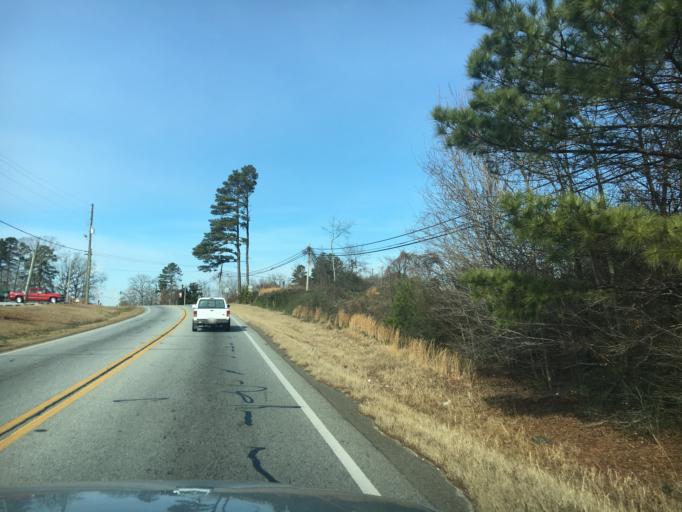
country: US
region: Georgia
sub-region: Jackson County
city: Braselton
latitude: 34.1038
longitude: -83.7618
